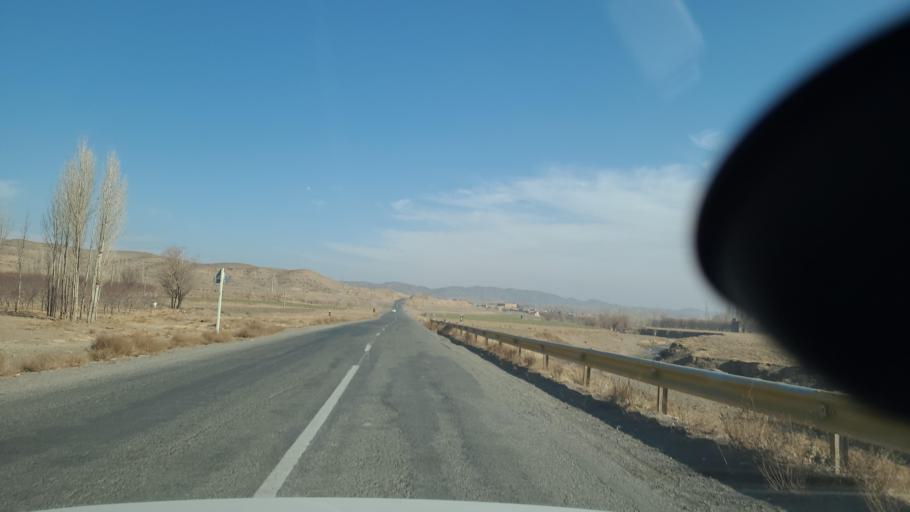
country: IR
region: Razavi Khorasan
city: Fariman
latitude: 35.5895
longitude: 59.6683
